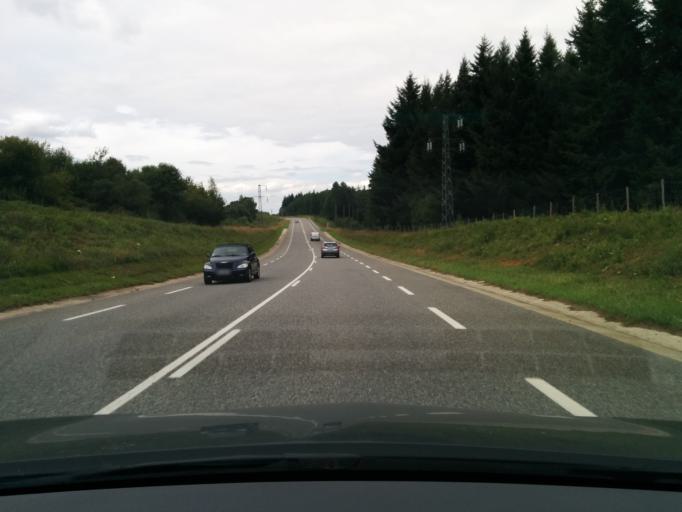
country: FR
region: Midi-Pyrenees
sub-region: Departement des Hautes-Pyrenees
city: La Barthe-de-Neste
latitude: 43.0704
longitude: 0.3609
